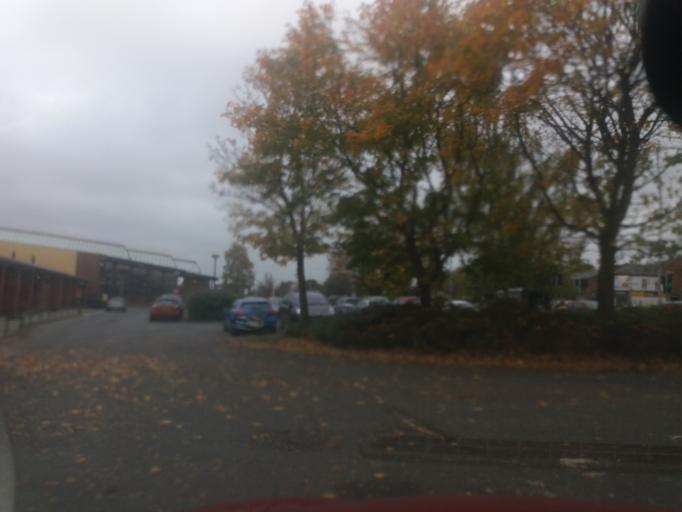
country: GB
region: England
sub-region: Lancashire
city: Chorley
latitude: 53.6600
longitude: -2.6278
